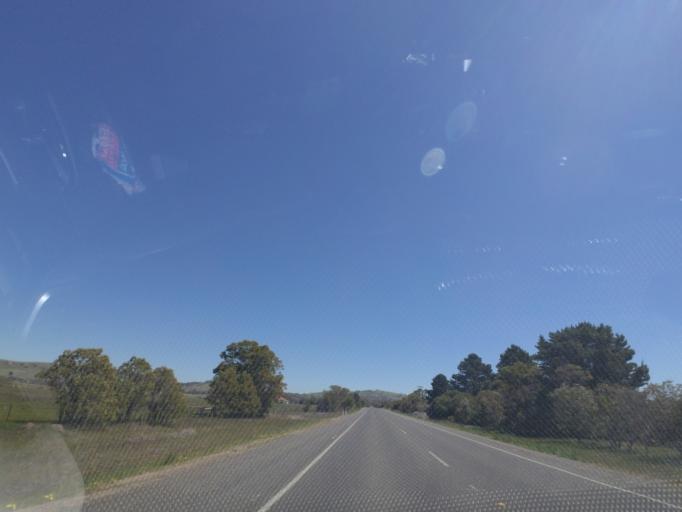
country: AU
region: Victoria
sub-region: Hume
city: Sunbury
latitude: -37.3075
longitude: 144.8397
